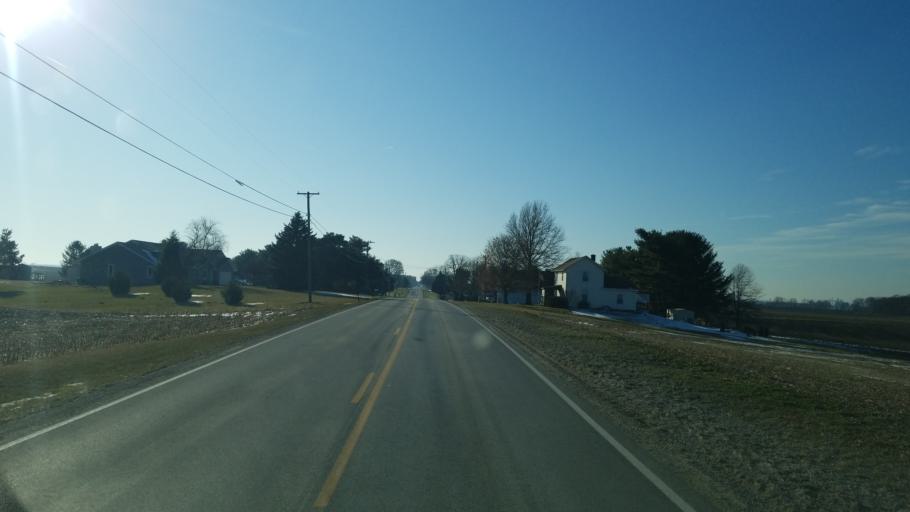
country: US
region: Ohio
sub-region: Sandusky County
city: Mount Carmel
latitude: 41.3121
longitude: -82.9118
